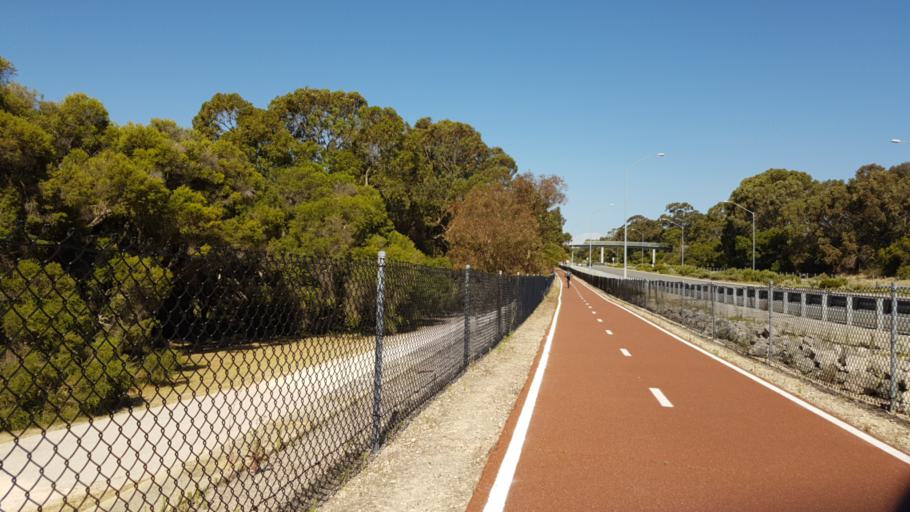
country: AU
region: Western Australia
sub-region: Stirling
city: Karrinyup
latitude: -31.8565
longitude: 115.7853
